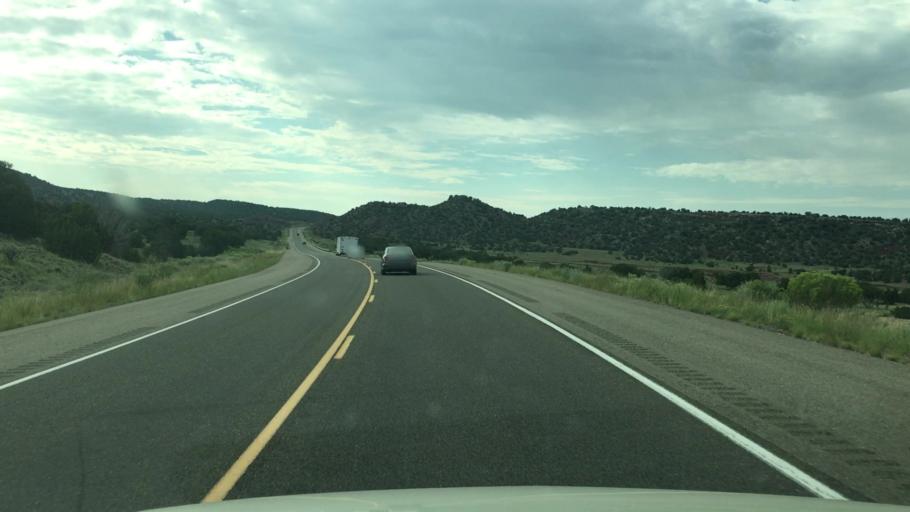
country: US
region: New Mexico
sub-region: Santa Fe County
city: Eldorado at Santa Fe
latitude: 35.2805
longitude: -105.8212
